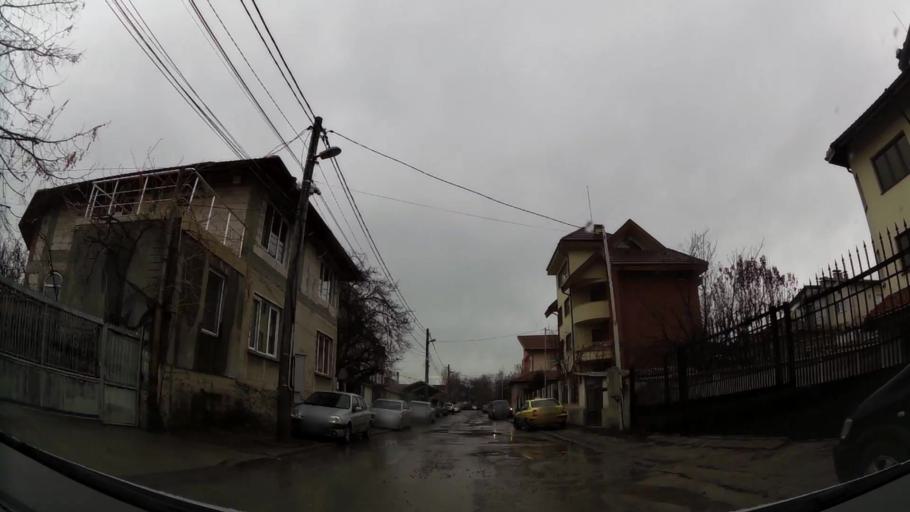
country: BG
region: Sofia-Capital
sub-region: Stolichna Obshtina
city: Sofia
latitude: 42.6256
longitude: 23.4099
